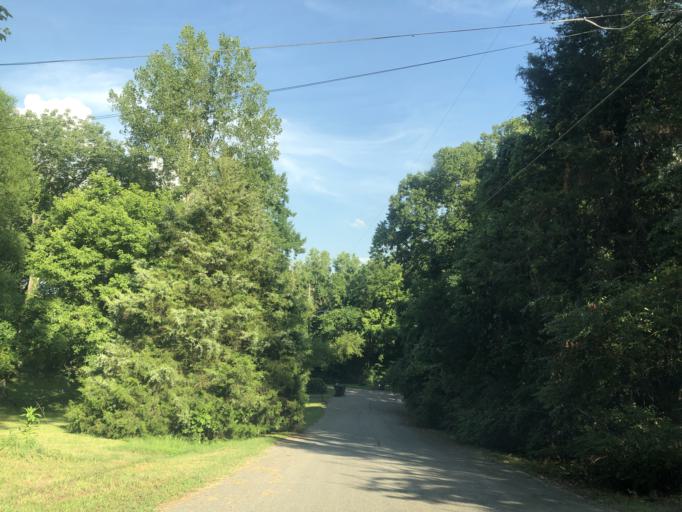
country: US
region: Tennessee
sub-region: Davidson County
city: Nashville
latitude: 36.2307
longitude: -86.8380
